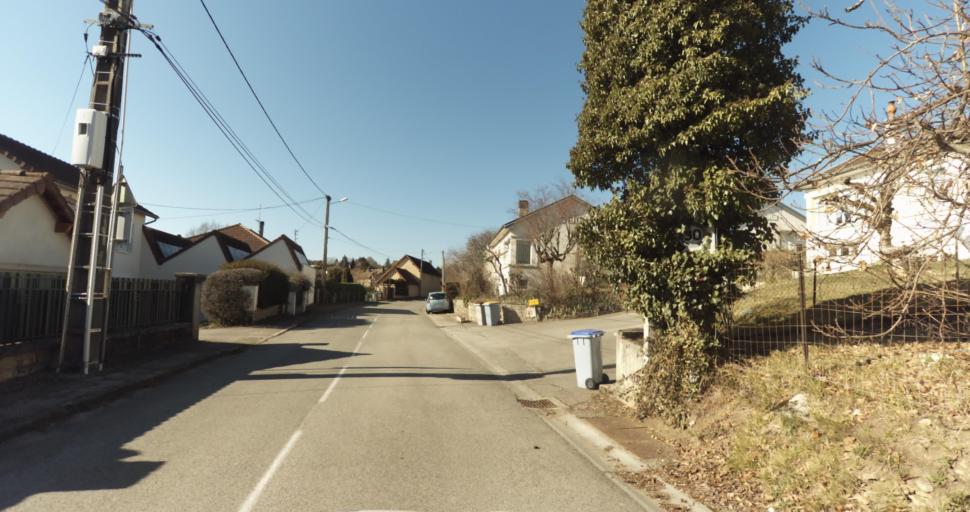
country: FR
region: Franche-Comte
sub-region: Departement du Jura
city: Lons-le-Saunier
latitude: 46.6780
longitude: 5.5426
